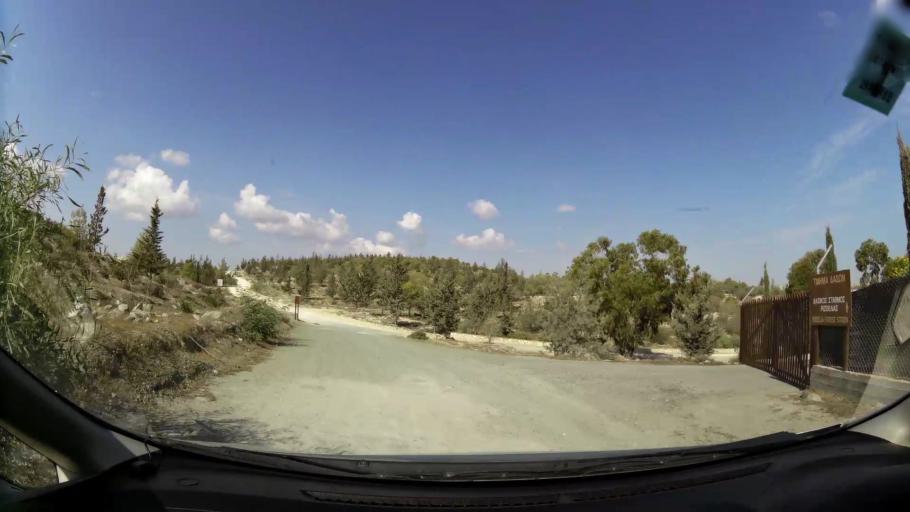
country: CY
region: Larnaka
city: Aradippou
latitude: 34.9448
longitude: 33.5769
